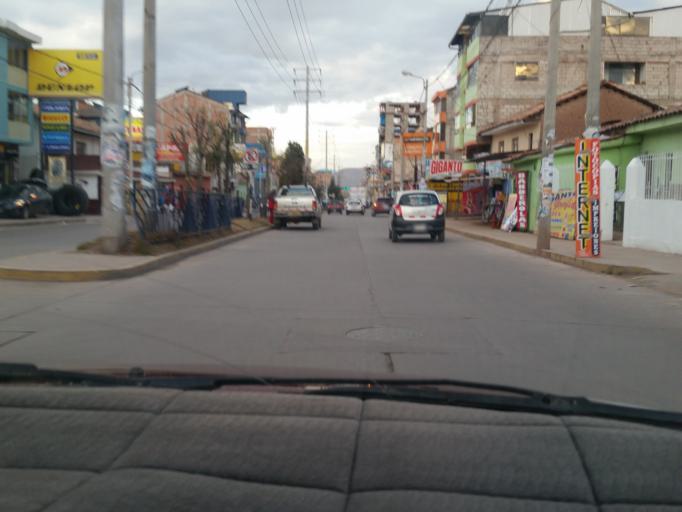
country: PE
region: Cusco
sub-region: Provincia de Cusco
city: Cusco
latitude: -13.5264
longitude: -71.9612
